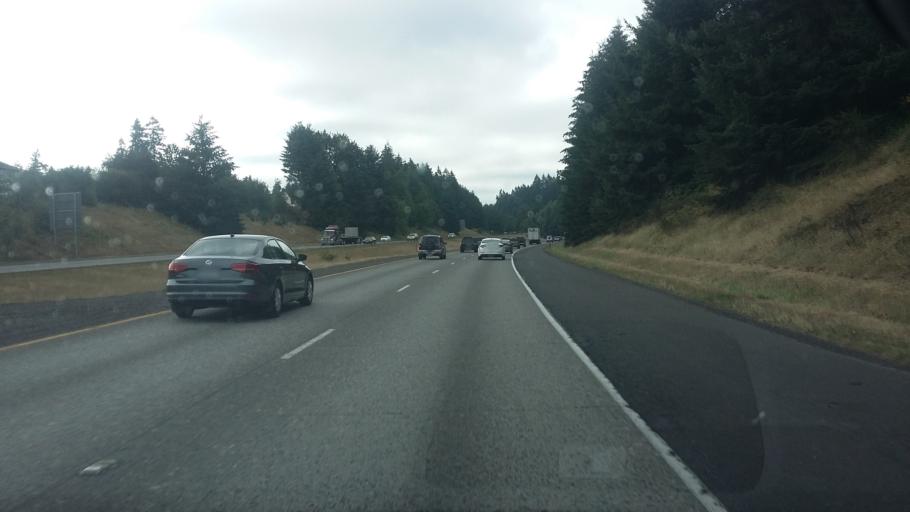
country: US
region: Washington
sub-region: Clark County
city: Salmon Creek
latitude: 45.7062
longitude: -122.6307
